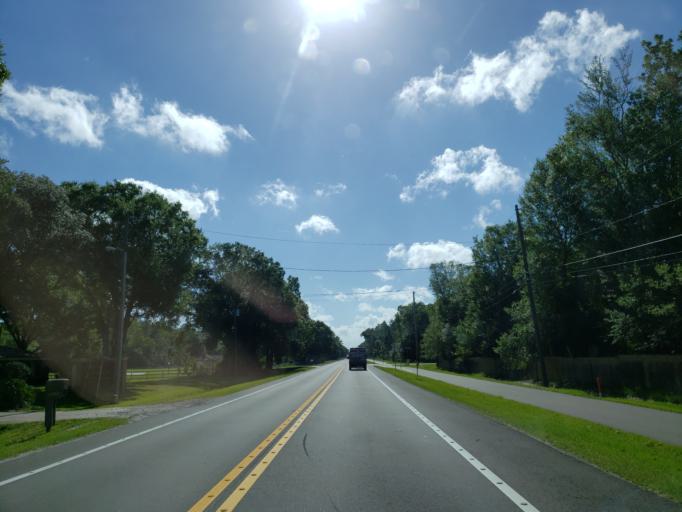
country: US
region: Florida
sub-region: Pasco County
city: Trinity
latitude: 28.1450
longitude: -82.6824
